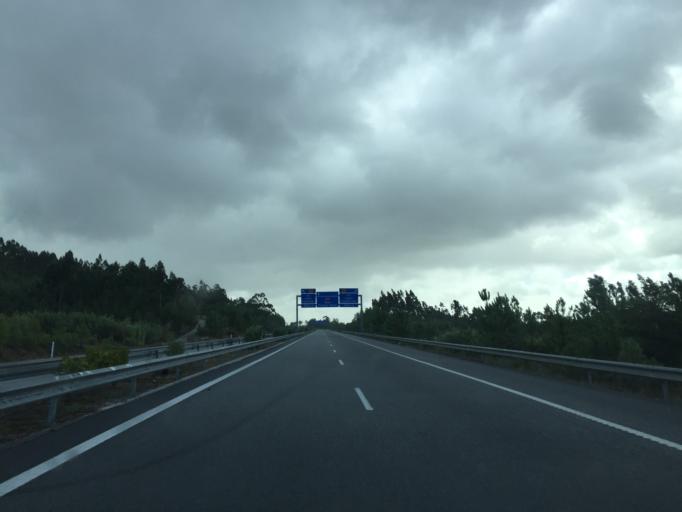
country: PT
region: Aveiro
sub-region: Mealhada
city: Pampilhosa do Botao
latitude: 40.2792
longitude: -8.5092
